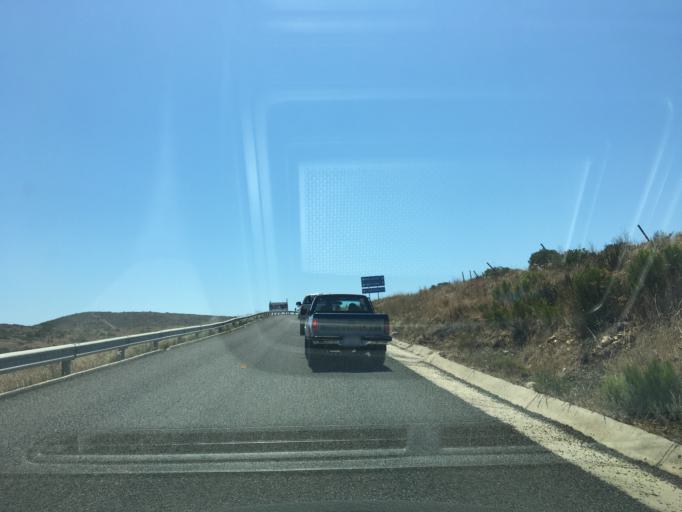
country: MX
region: Baja California
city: El Sauzal
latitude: 31.9943
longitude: -116.6884
